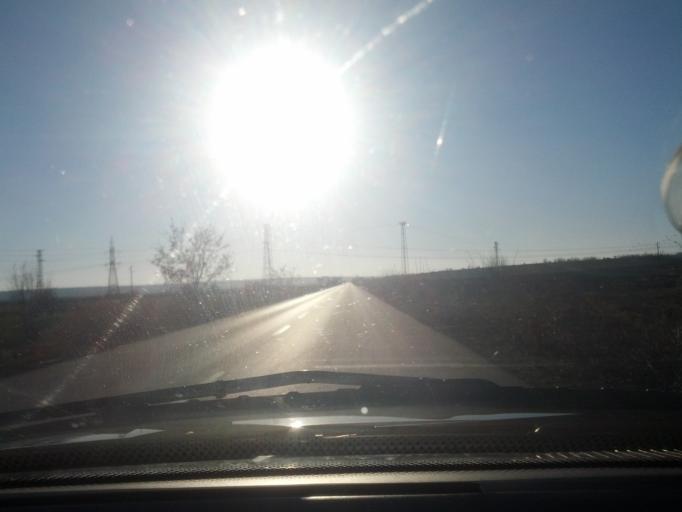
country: BG
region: Vratsa
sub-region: Obshtina Miziya
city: Miziya
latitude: 43.6734
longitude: 23.7919
